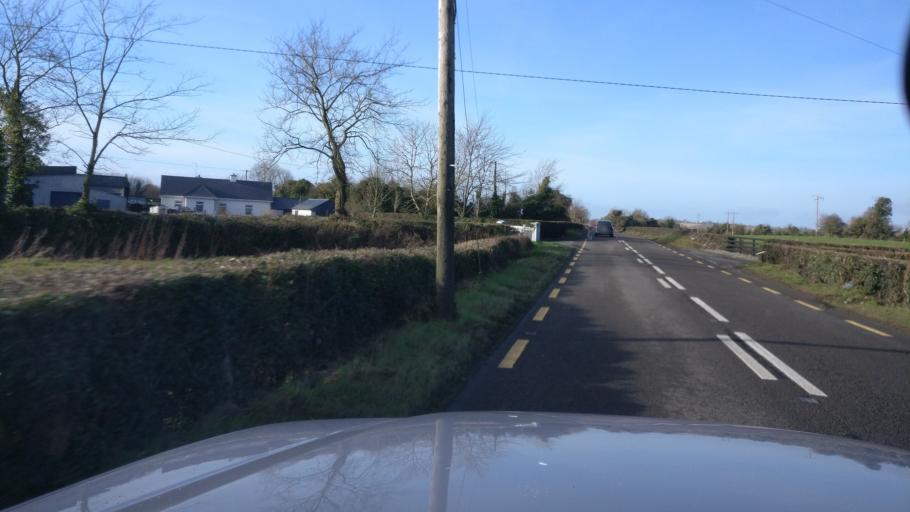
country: IE
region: Leinster
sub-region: Laois
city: Mountmellick
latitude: 53.1718
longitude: -7.3823
